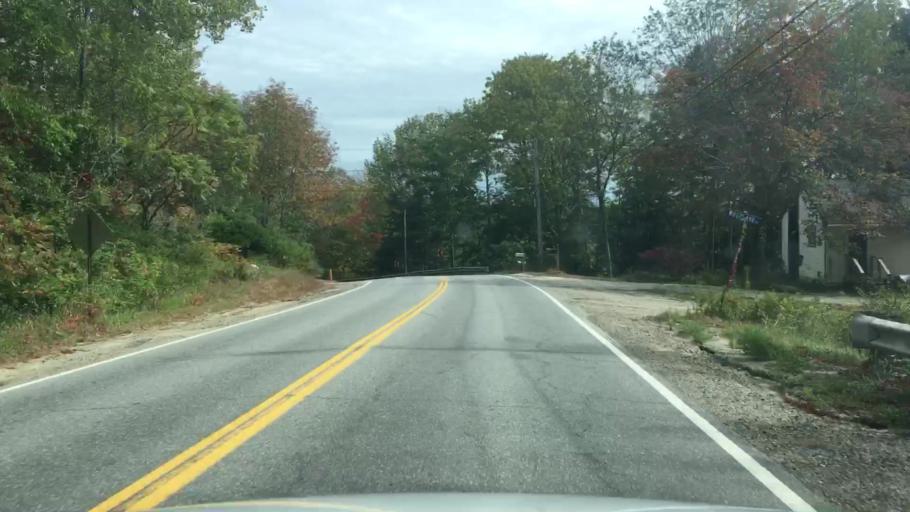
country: US
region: Maine
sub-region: Sagadahoc County
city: Topsham
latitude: 43.9344
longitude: -70.0154
